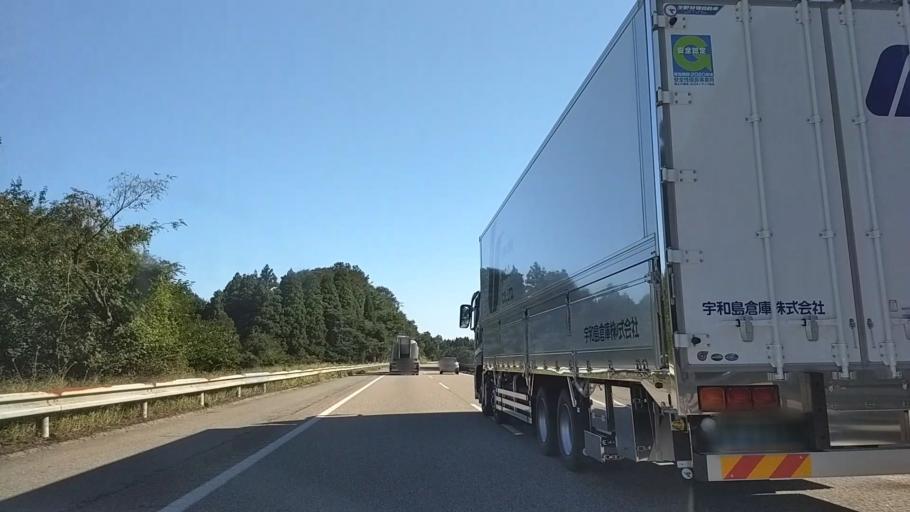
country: JP
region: Toyama
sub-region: Oyabe Shi
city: Oyabe
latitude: 36.6102
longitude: 136.8104
